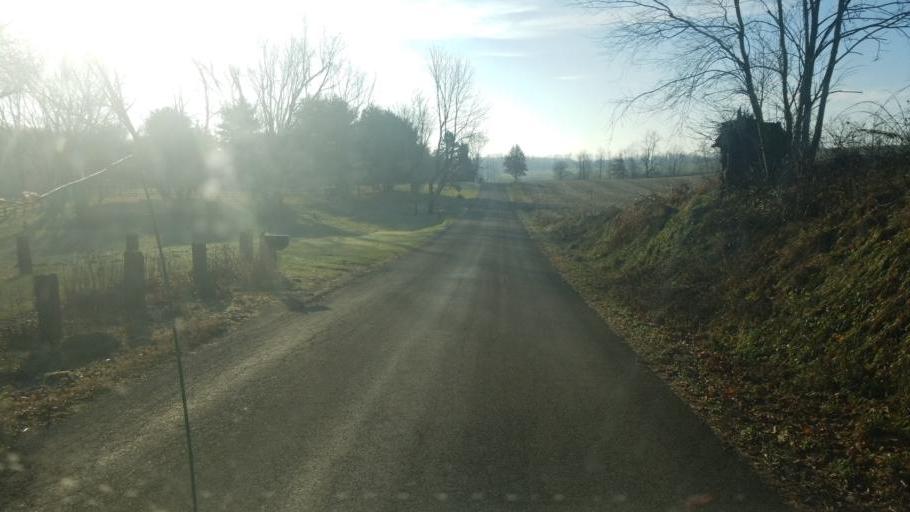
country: US
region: Ohio
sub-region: Knox County
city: Gambier
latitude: 40.4287
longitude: -82.3867
